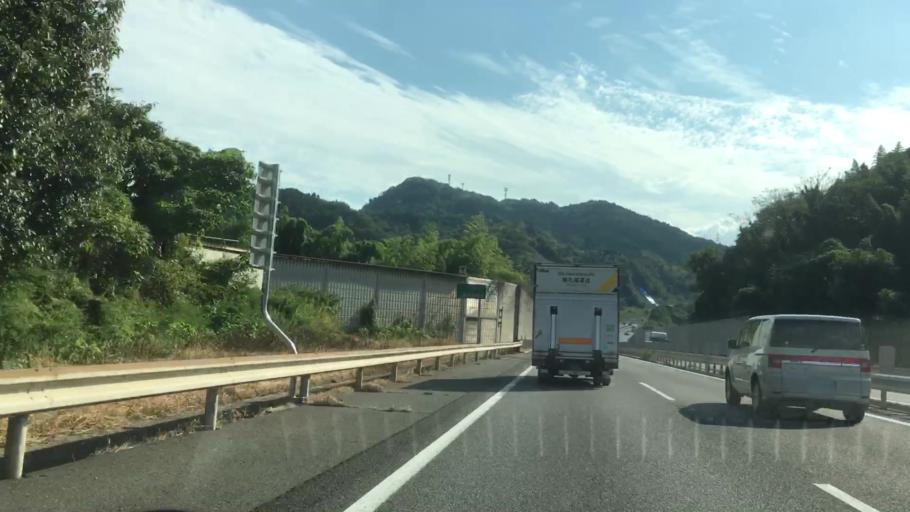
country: JP
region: Yamaguchi
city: Otake
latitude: 34.2379
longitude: 132.2143
